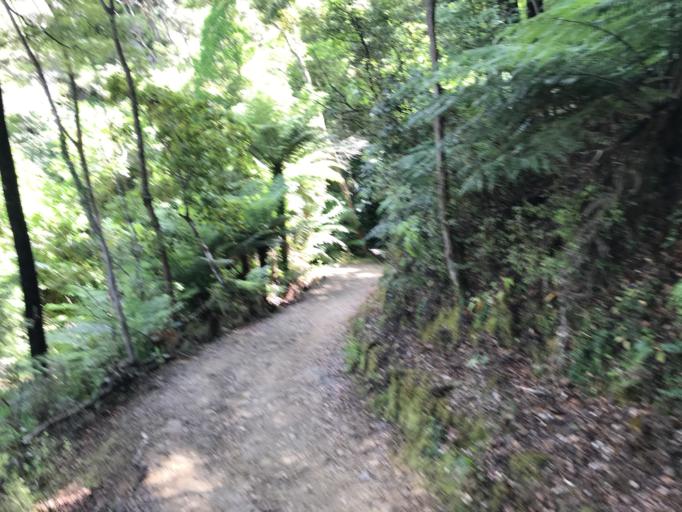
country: NZ
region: Marlborough
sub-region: Marlborough District
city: Picton
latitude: -41.2555
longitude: 173.9386
